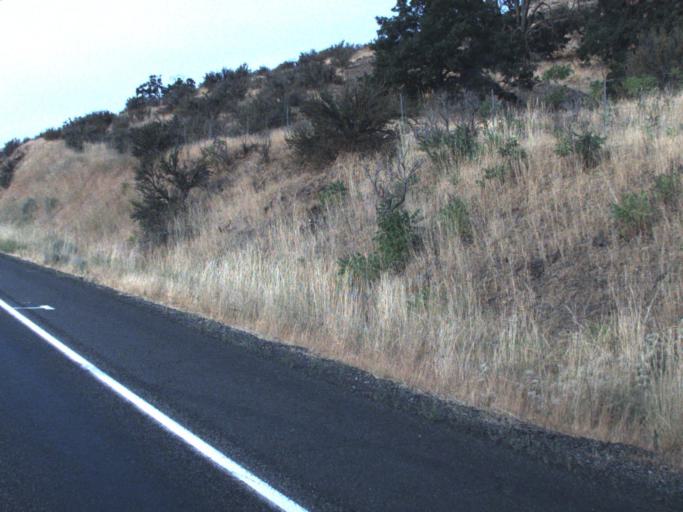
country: US
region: Washington
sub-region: Yakima County
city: Toppenish
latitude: 46.0985
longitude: -120.5459
